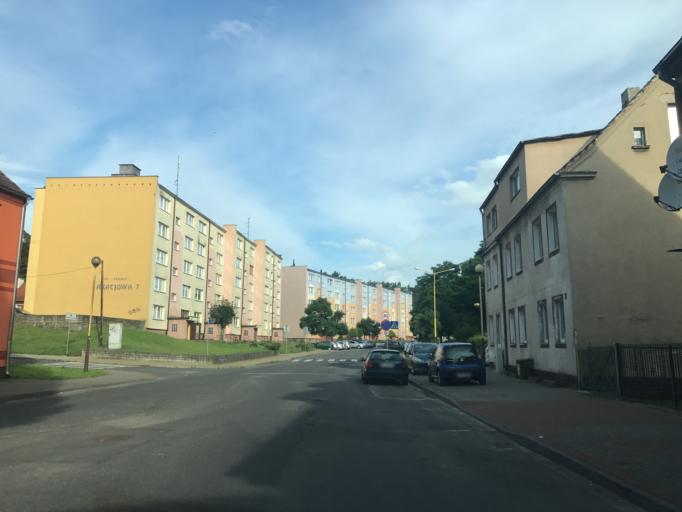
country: PL
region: West Pomeranian Voivodeship
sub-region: Powiat goleniowski
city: Goleniow
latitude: 53.5617
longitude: 14.8196
